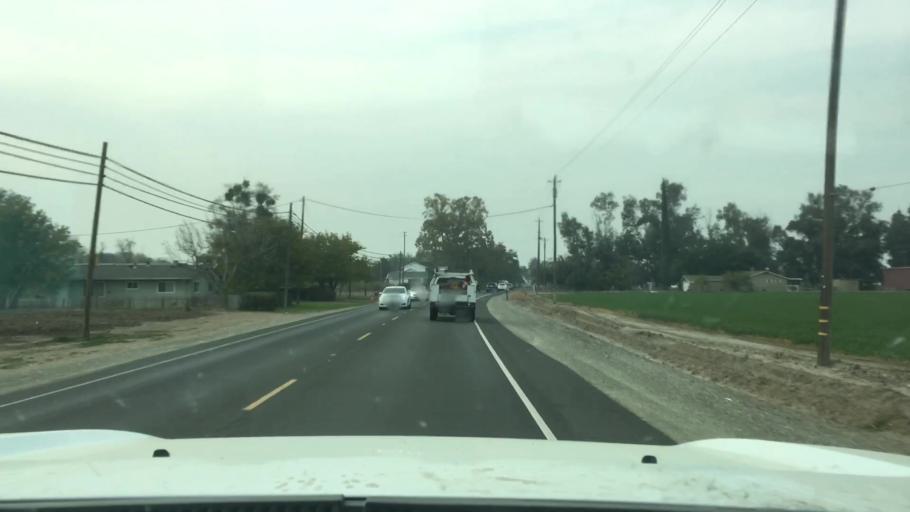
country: US
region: California
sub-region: San Joaquin County
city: French Camp
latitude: 37.8709
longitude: -121.2490
